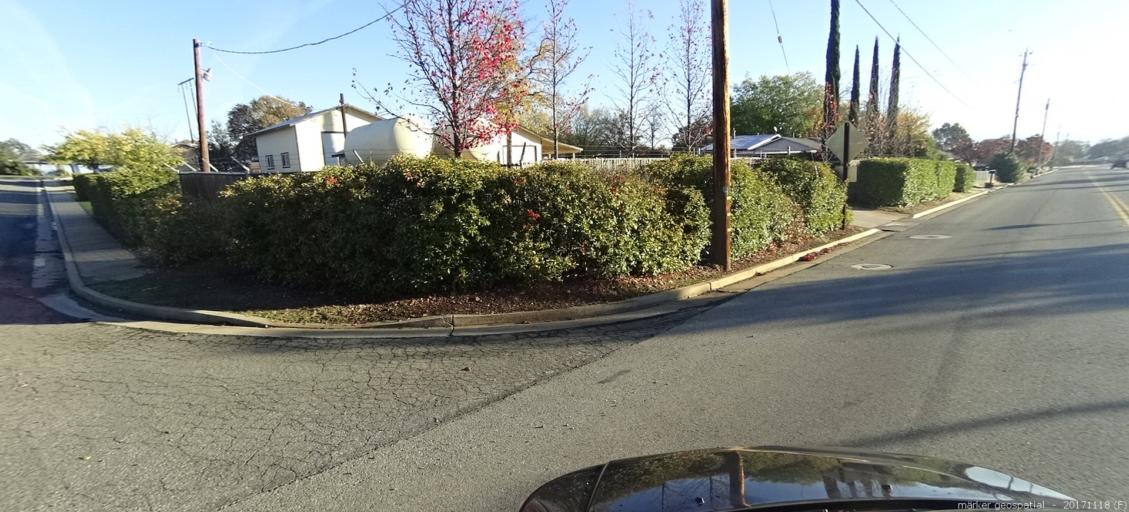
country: US
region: California
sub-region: Shasta County
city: Cottonwood
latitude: 40.3978
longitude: -122.2872
